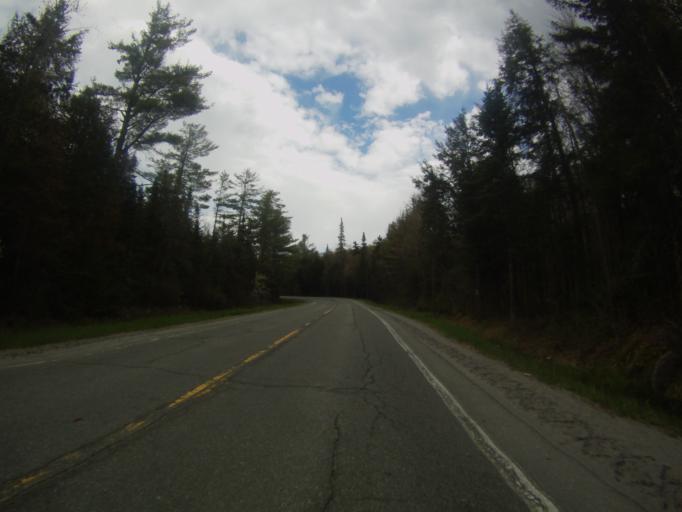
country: US
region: New York
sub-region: Essex County
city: Mineville
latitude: 44.0982
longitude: -73.5650
